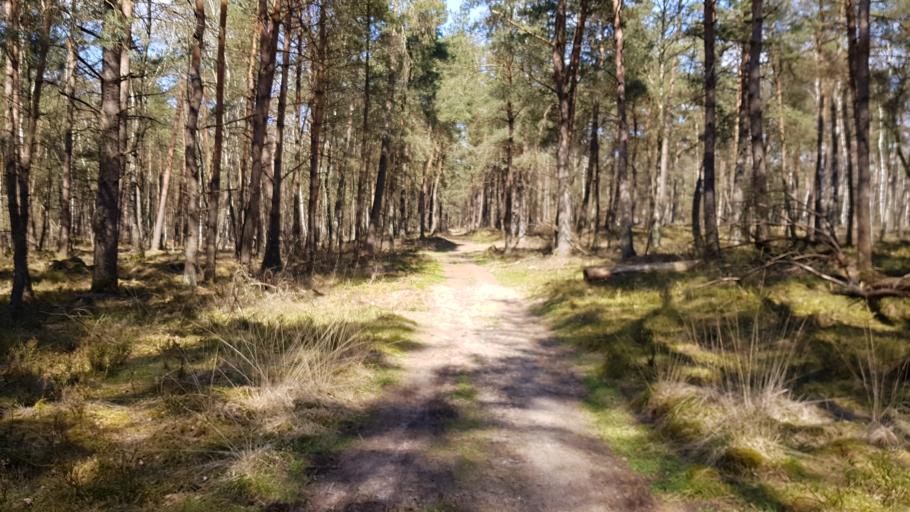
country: NL
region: Gelderland
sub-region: Gemeente Apeldoorn
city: Loenen
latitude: 52.0688
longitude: 6.0075
